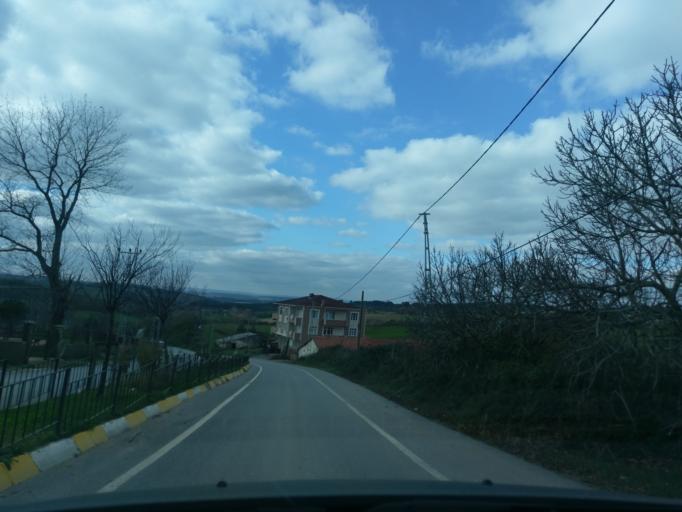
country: TR
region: Istanbul
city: Durusu
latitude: 41.3173
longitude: 28.7189
